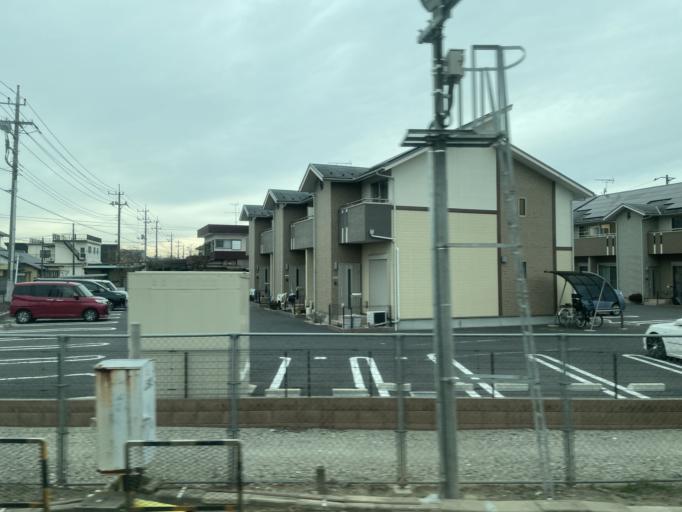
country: JP
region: Saitama
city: Kukichuo
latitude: 36.1001
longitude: 139.6786
